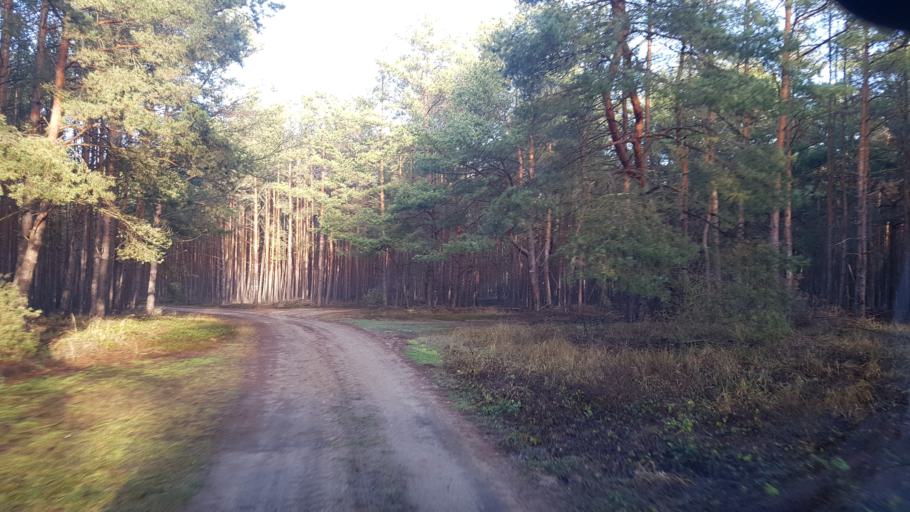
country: DE
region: Brandenburg
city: Schilda
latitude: 51.6213
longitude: 13.3913
